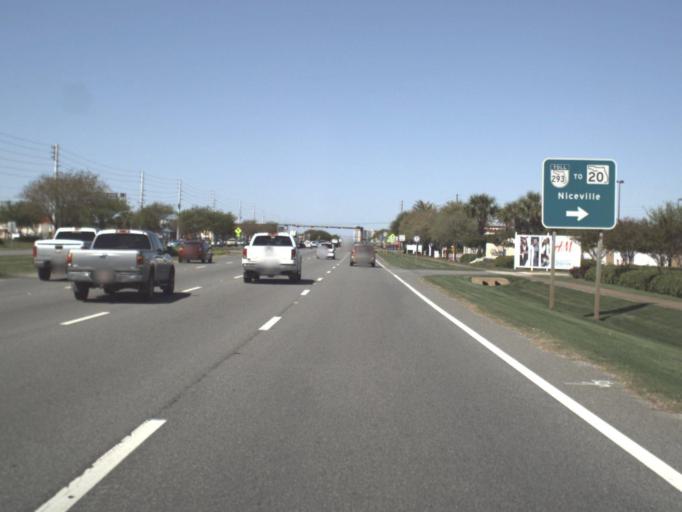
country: US
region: Florida
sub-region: Walton County
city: Miramar Beach
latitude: 30.3895
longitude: -86.4234
